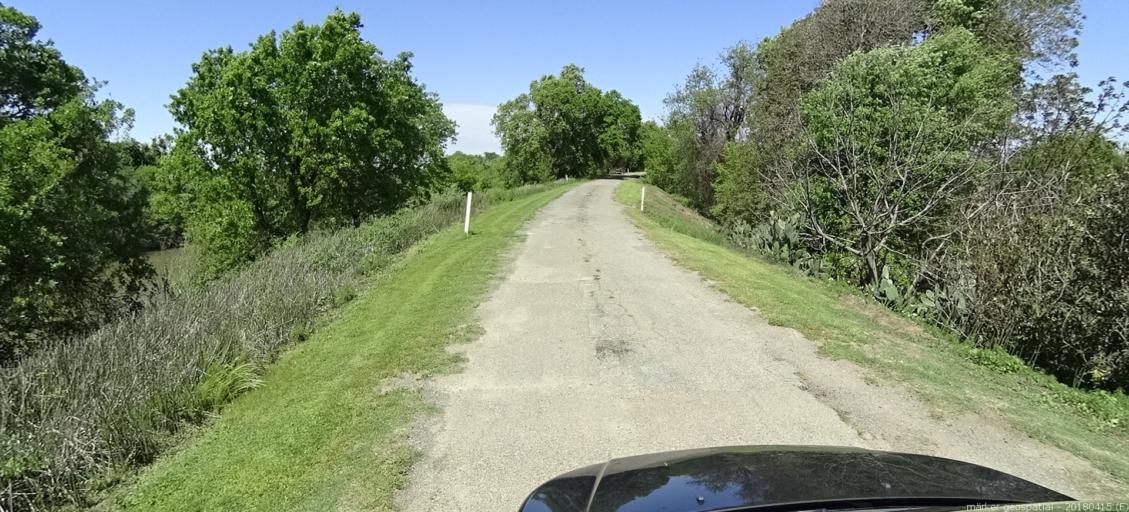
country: US
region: California
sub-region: Sacramento County
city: Walnut Grove
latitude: 38.2699
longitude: -121.6036
